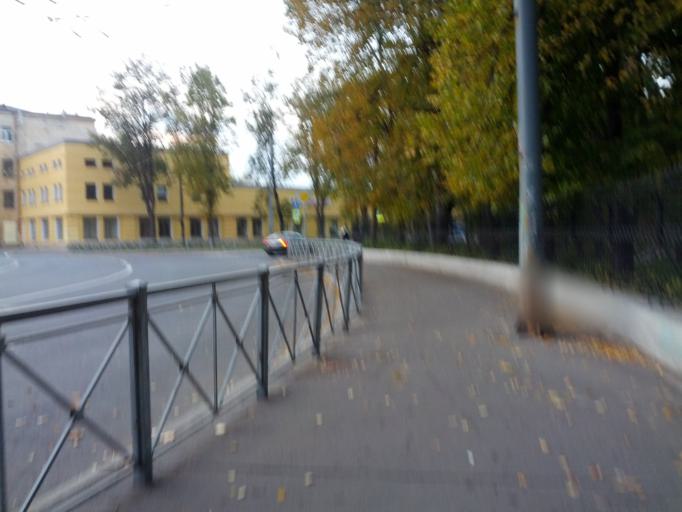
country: RU
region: Leningrad
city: Krestovskiy ostrov
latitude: 59.9622
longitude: 30.2541
